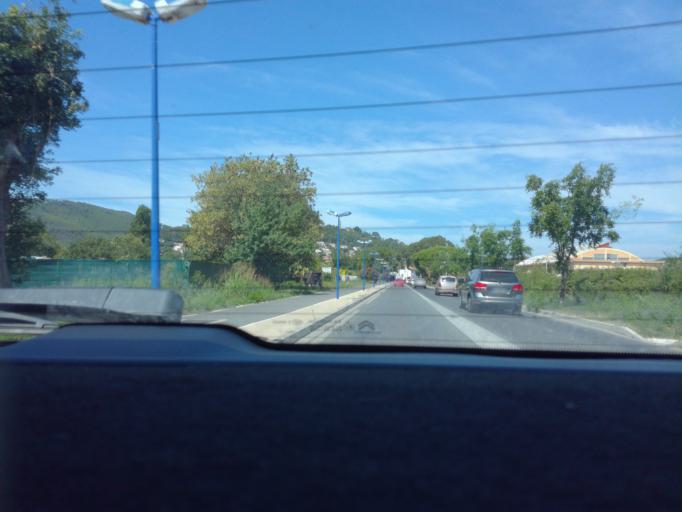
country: FR
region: Provence-Alpes-Cote d'Azur
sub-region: Departement du Var
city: Hyeres
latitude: 43.0934
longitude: 6.1393
